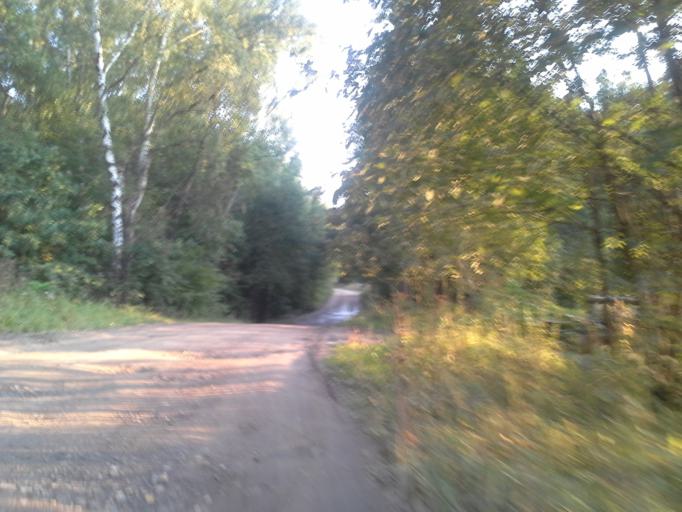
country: RU
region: Moskovskaya
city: Dubrovitsy
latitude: 55.5047
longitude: 37.4290
